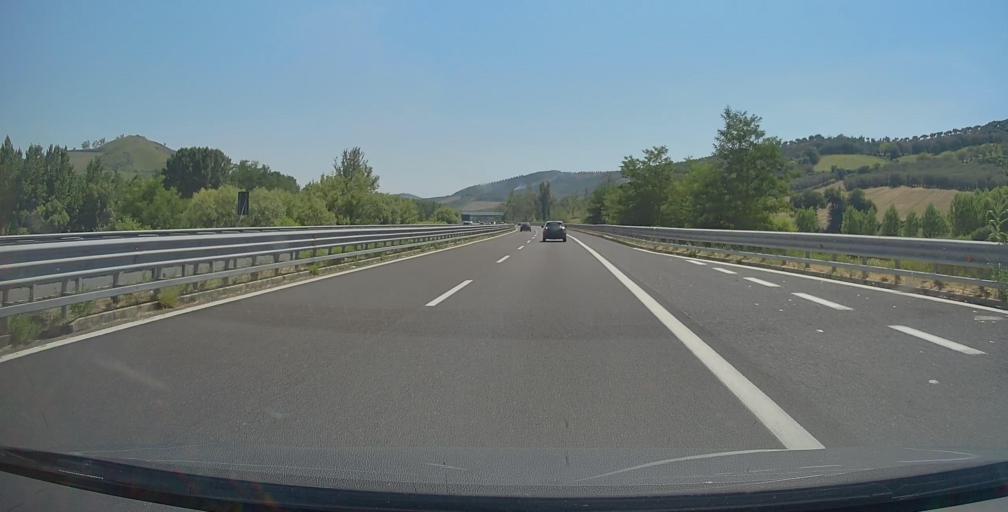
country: IT
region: Calabria
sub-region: Provincia di Vibo-Valentia
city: Francica
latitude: 38.6029
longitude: 16.1440
